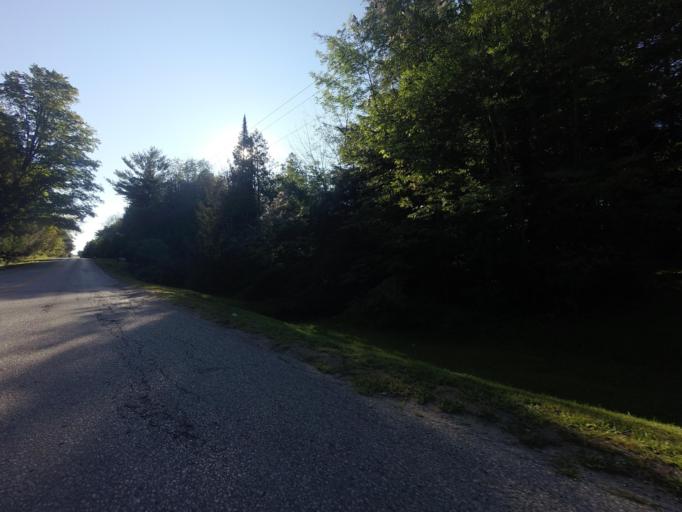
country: CA
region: Ontario
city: Bradford West Gwillimbury
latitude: 44.0491
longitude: -79.7416
